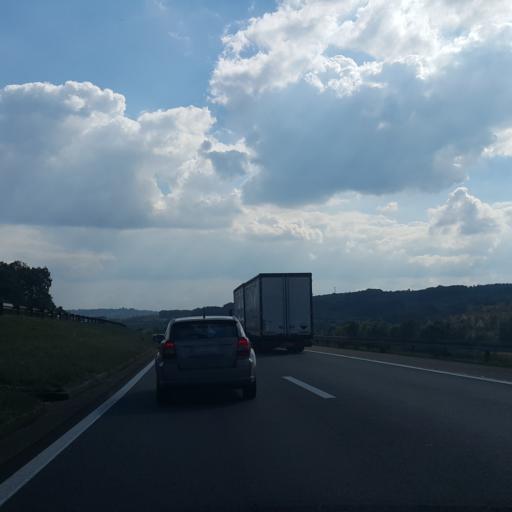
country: RS
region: Central Serbia
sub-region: Belgrade
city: Sopot
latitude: 44.5945
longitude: 20.6395
